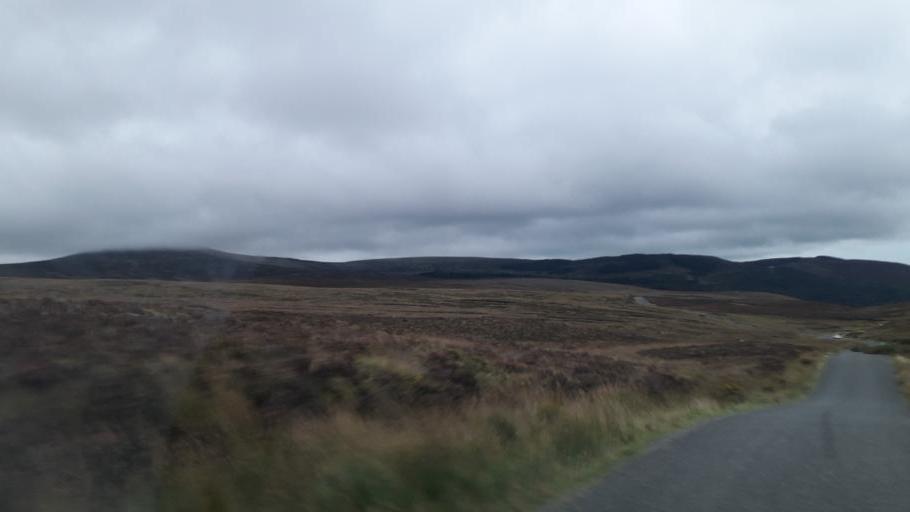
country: IE
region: Leinster
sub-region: Wicklow
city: Enniskerry
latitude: 53.1298
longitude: -6.2947
